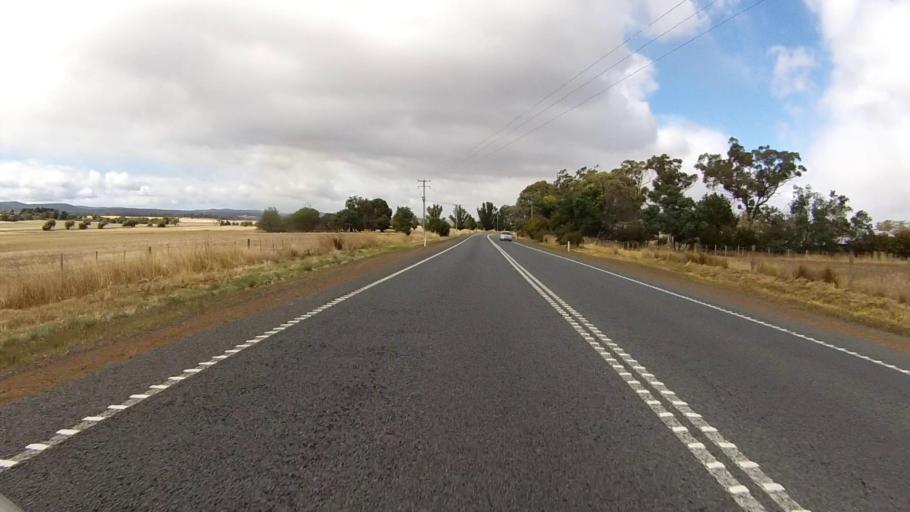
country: AU
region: Tasmania
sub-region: Northern Midlands
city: Evandale
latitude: -41.9831
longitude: 147.5061
